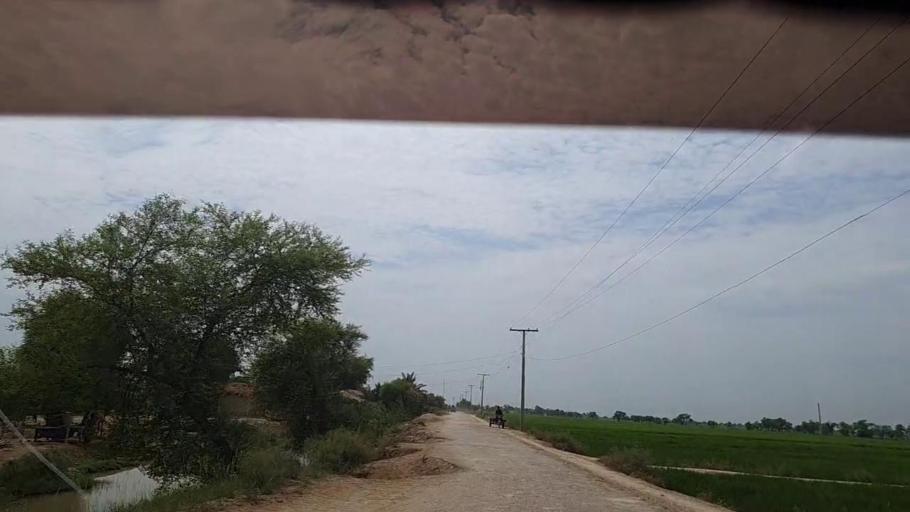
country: PK
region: Sindh
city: Thul
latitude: 28.2428
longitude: 68.7478
